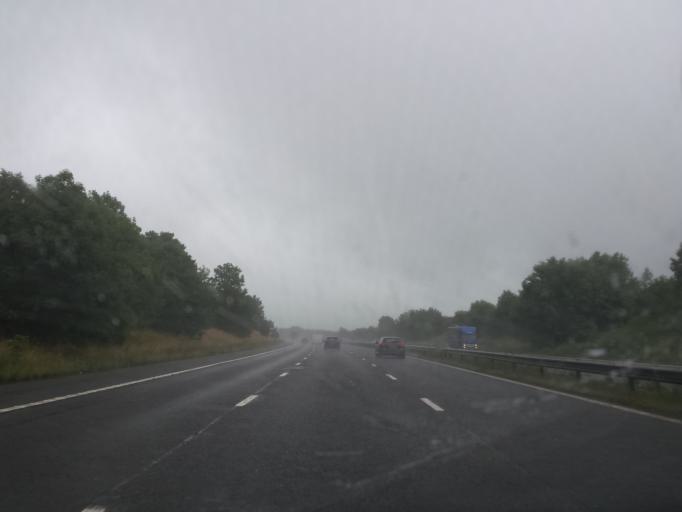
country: GB
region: England
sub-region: Leicestershire
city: Markfield
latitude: 52.6704
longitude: -1.2806
